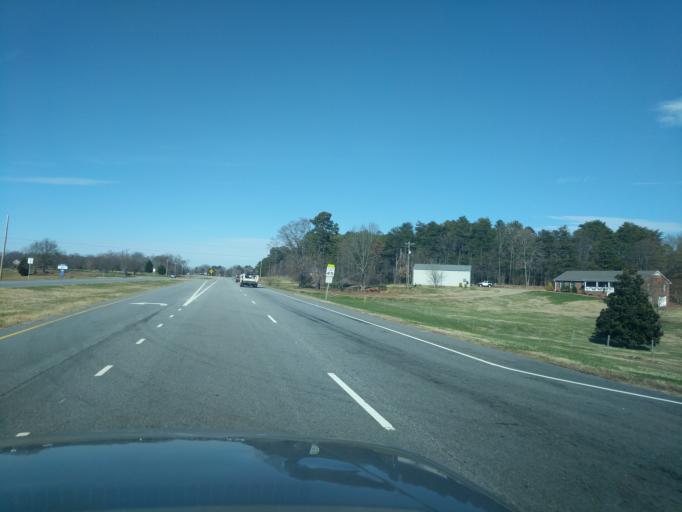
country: US
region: North Carolina
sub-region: Rutherford County
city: Forest City
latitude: 35.2727
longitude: -81.8932
